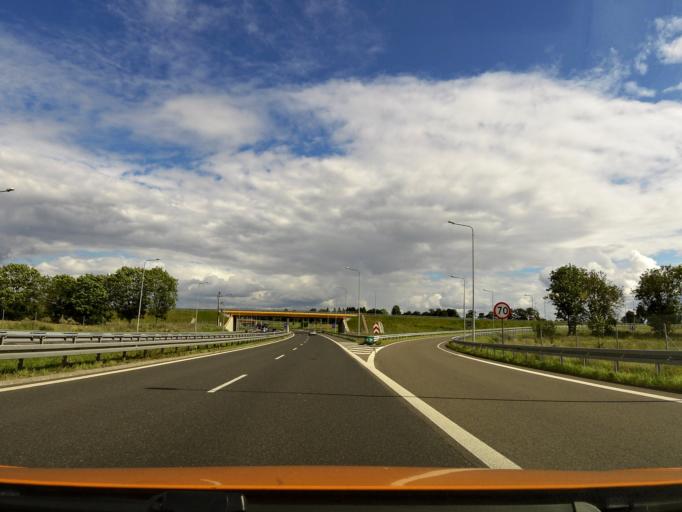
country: PL
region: West Pomeranian Voivodeship
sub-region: Powiat goleniowski
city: Nowogard
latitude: 53.6907
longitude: 15.1347
